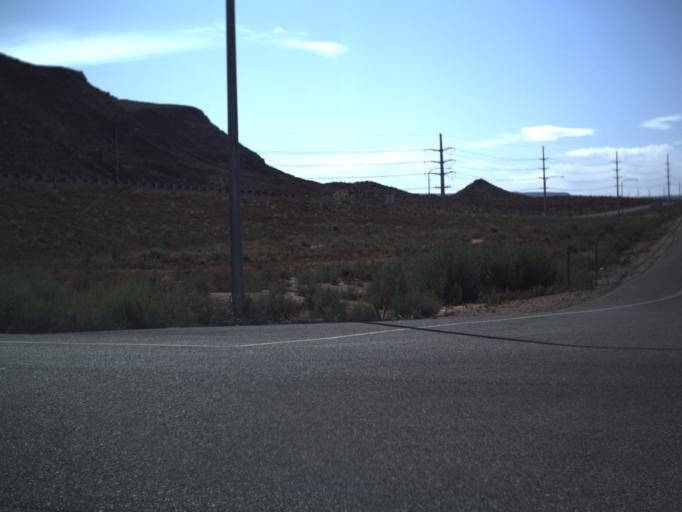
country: US
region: Utah
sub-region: Washington County
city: Washington
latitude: 37.0593
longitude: -113.4867
